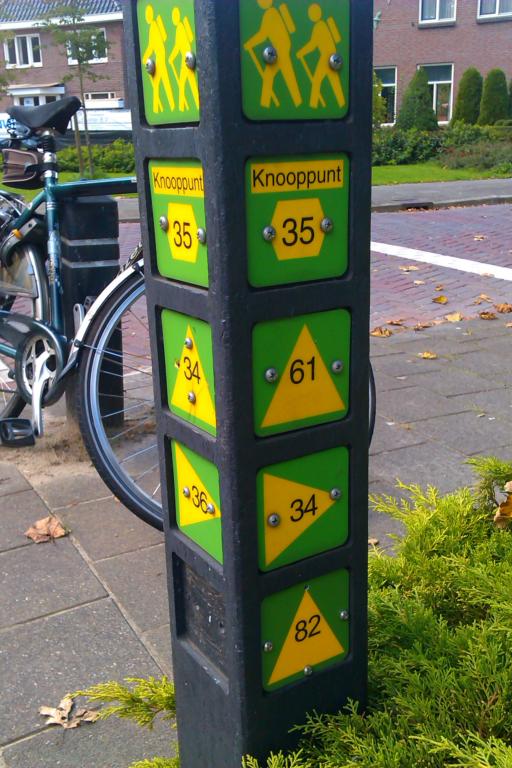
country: NL
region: North Brabant
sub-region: Gemeente Valkenswaard
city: Valkenswaard
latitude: 51.3509
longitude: 5.4374
